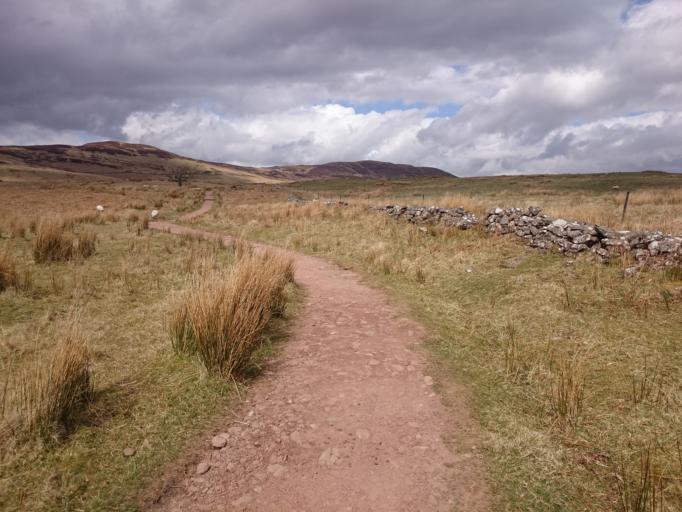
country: GB
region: Scotland
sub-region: West Dunbartonshire
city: Balloch
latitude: 56.0969
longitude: -4.4913
